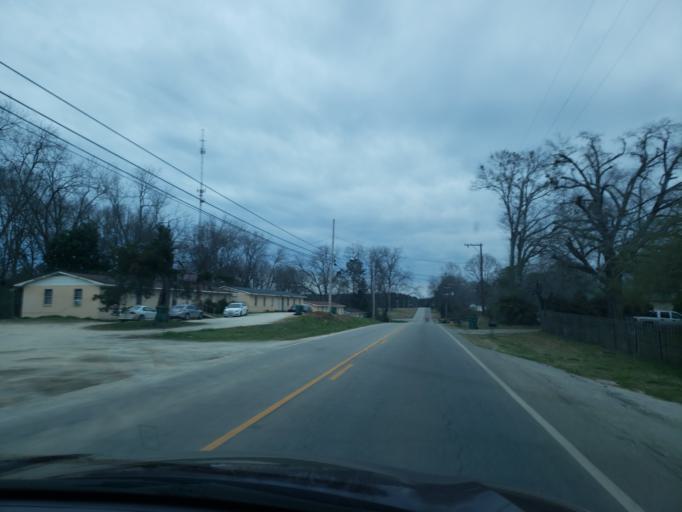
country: US
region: Alabama
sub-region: Chambers County
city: Lafayette
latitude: 32.9139
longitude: -85.4001
